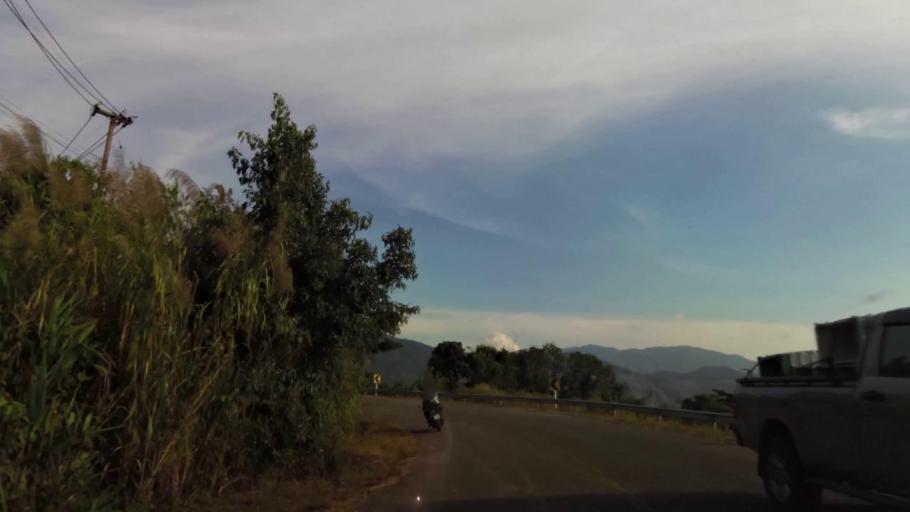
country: TH
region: Chiang Rai
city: Khun Tan
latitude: 19.8529
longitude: 100.3764
